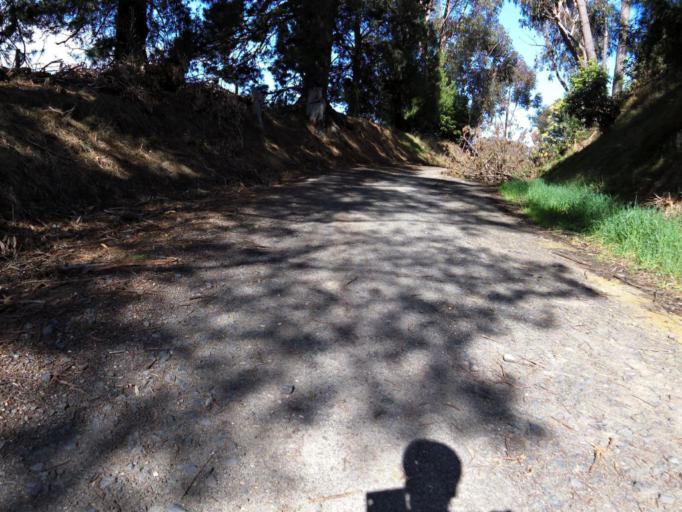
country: AU
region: Victoria
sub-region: Baw Baw
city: Warragul
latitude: -38.0368
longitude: 145.9521
